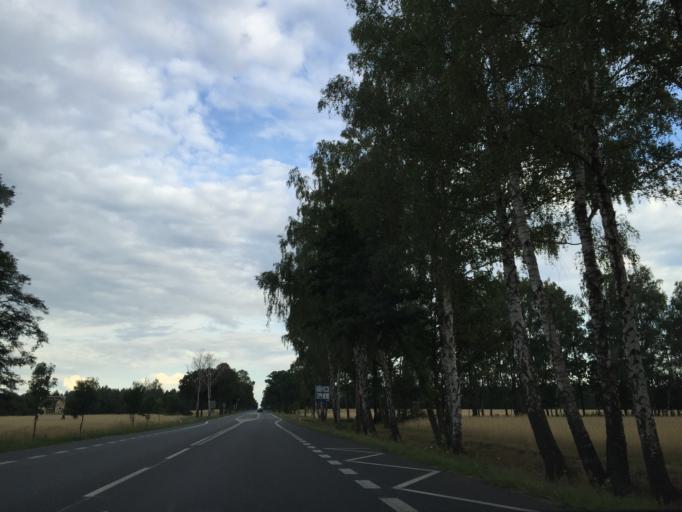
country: PL
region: Lublin Voivodeship
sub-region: Powiat lubartowski
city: Firlej
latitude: 51.5961
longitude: 22.4761
